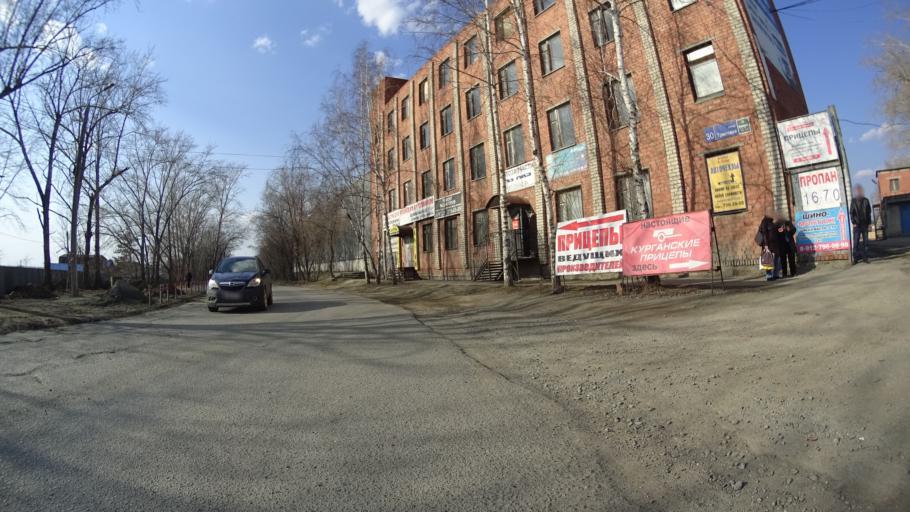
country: RU
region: Chelyabinsk
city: Novosineglazovskiy
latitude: 55.1033
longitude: 61.3436
